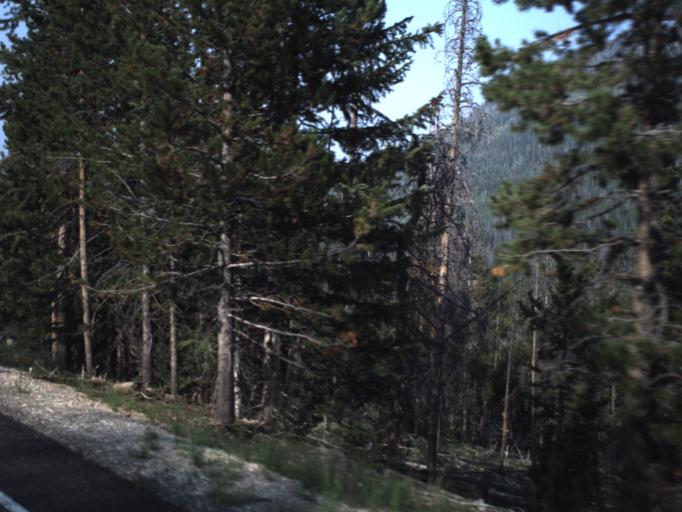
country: US
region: Utah
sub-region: Summit County
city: Kamas
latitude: 40.7772
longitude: -110.8847
